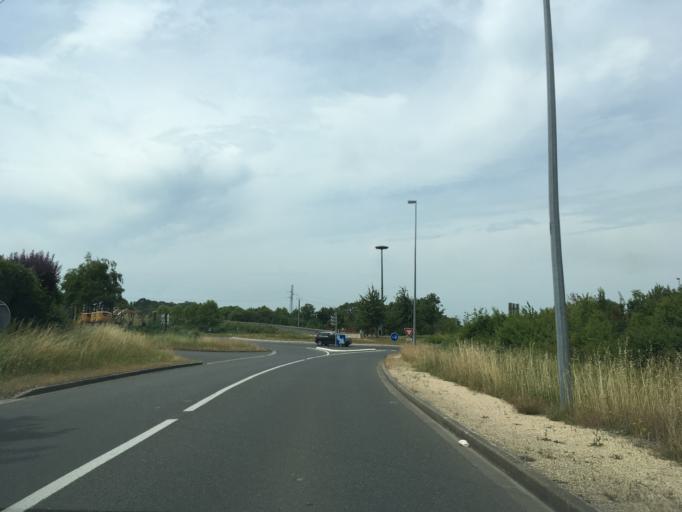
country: FR
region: Poitou-Charentes
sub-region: Departement des Deux-Sevres
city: Niort
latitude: 46.2967
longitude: -0.4646
